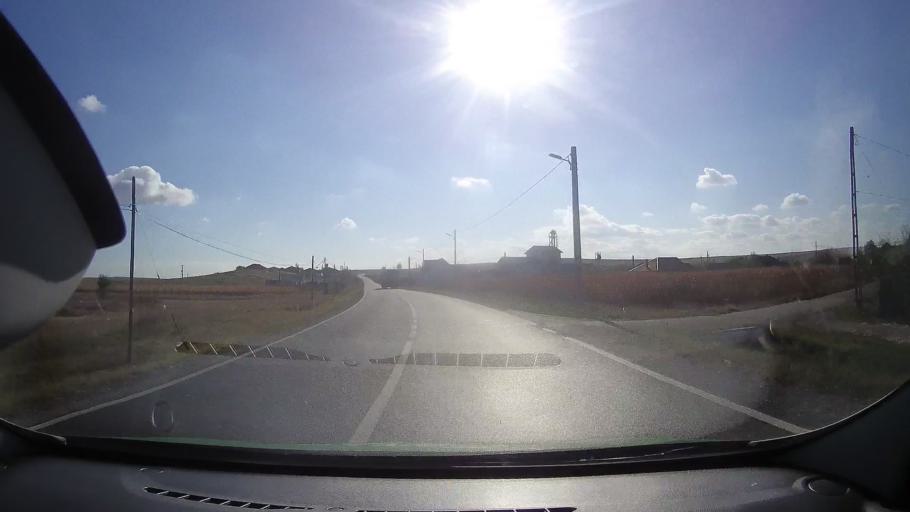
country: RO
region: Tulcea
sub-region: Comuna Baia
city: Baia
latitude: 44.7210
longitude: 28.6793
